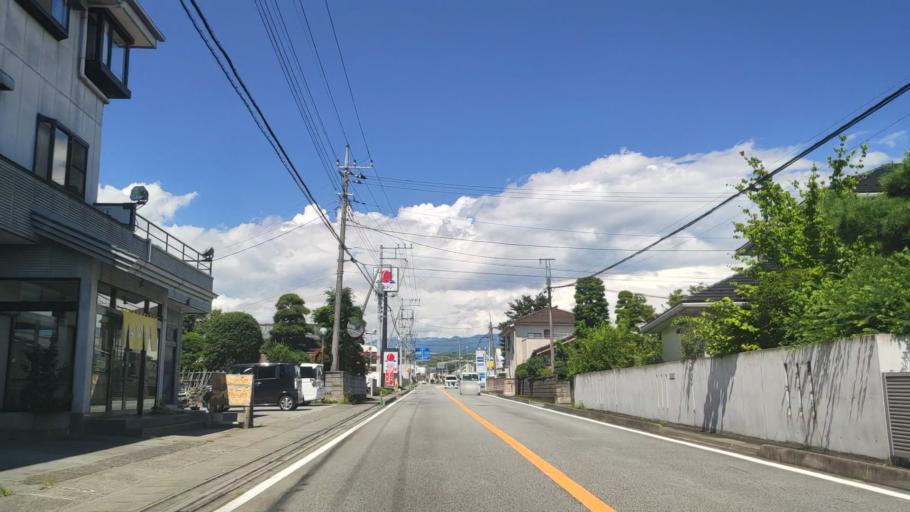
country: JP
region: Yamanashi
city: Isawa
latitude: 35.6795
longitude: 138.6595
